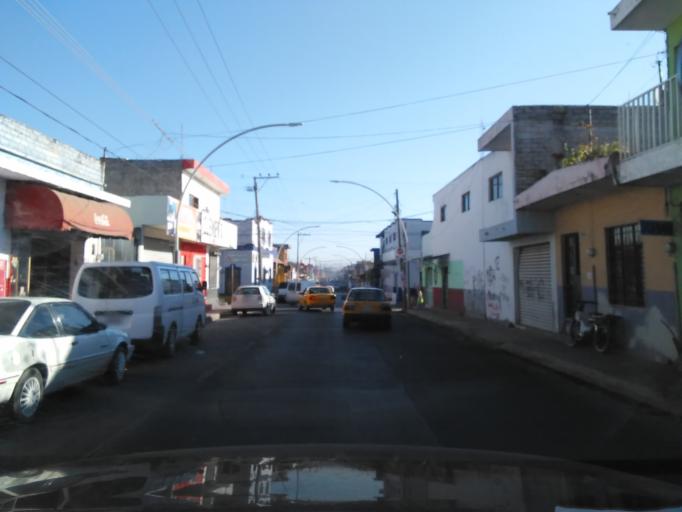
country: MX
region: Nayarit
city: Tepic
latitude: 21.5169
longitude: -104.9084
